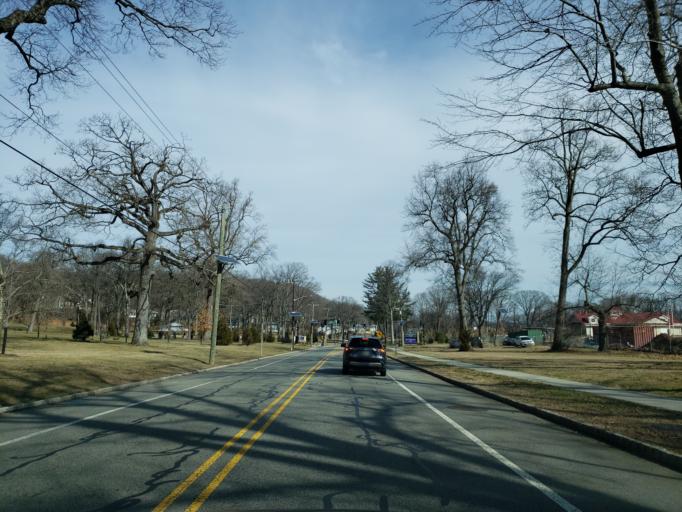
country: US
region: New Jersey
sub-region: Essex County
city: Cedar Grove
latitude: 40.8531
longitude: -74.2430
